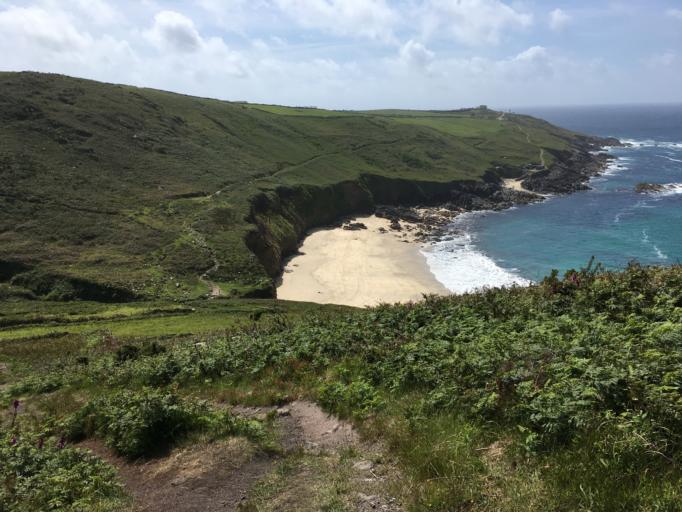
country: GB
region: England
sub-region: Cornwall
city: Saint Just
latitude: 50.1645
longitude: -5.6543
